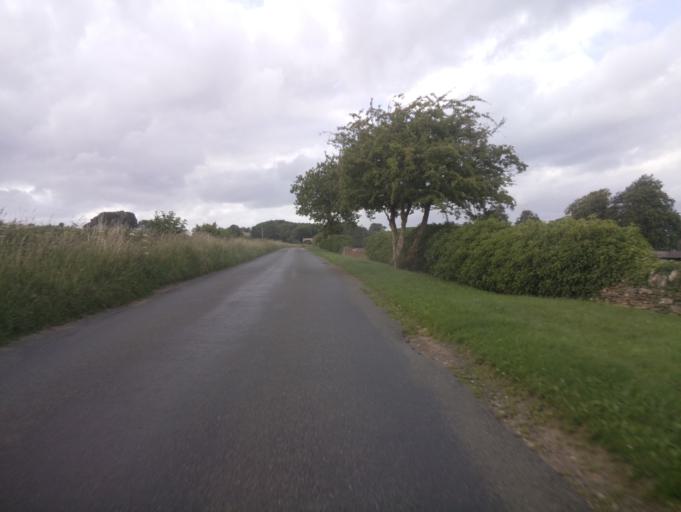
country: GB
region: England
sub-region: Gloucestershire
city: Donnington
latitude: 51.9850
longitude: -1.7543
